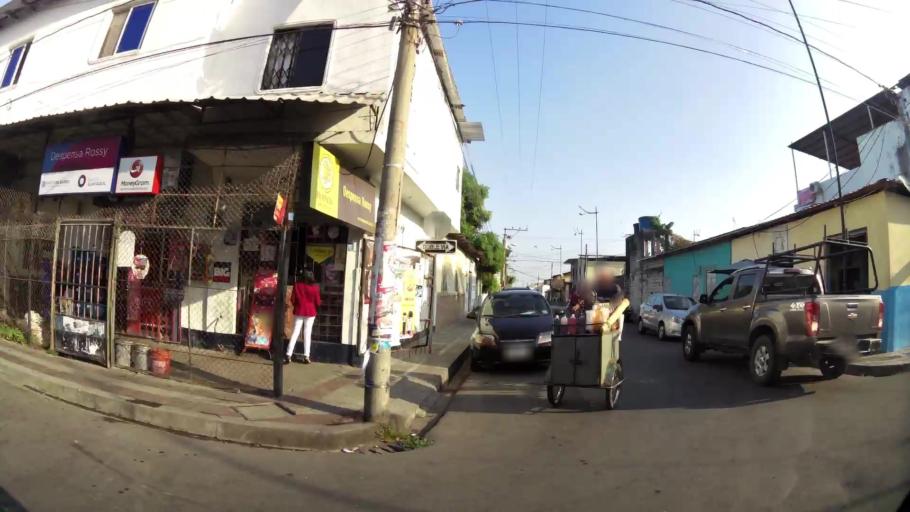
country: EC
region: Guayas
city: Eloy Alfaro
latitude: -2.1773
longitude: -79.8550
